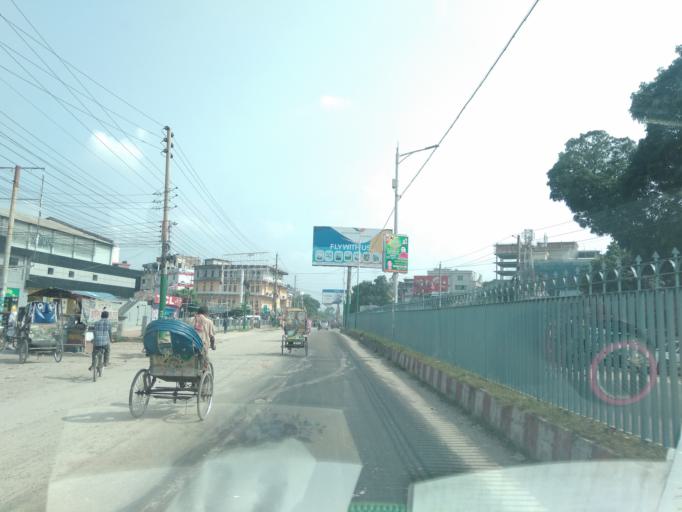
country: BD
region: Rangpur Division
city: Rangpur
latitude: 25.7615
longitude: 89.2315
